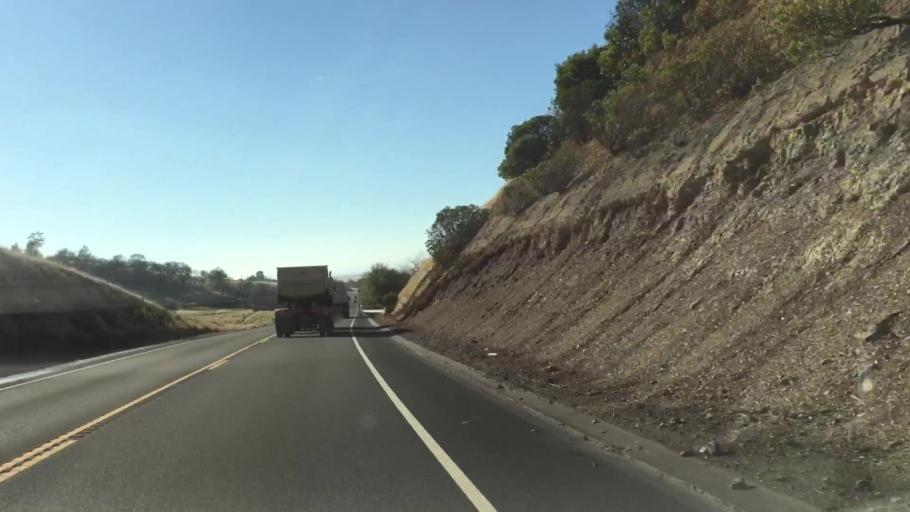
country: US
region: California
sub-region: Butte County
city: Oroville
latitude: 39.6398
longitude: -121.5742
